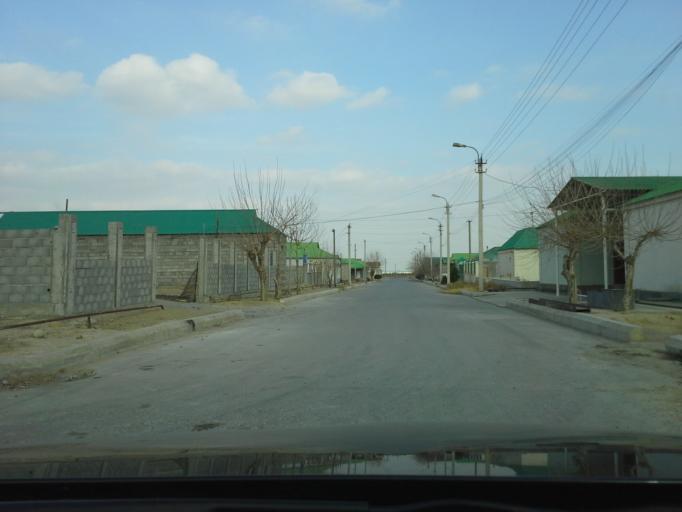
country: TM
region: Ahal
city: Abadan
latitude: 38.0430
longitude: 58.2722
